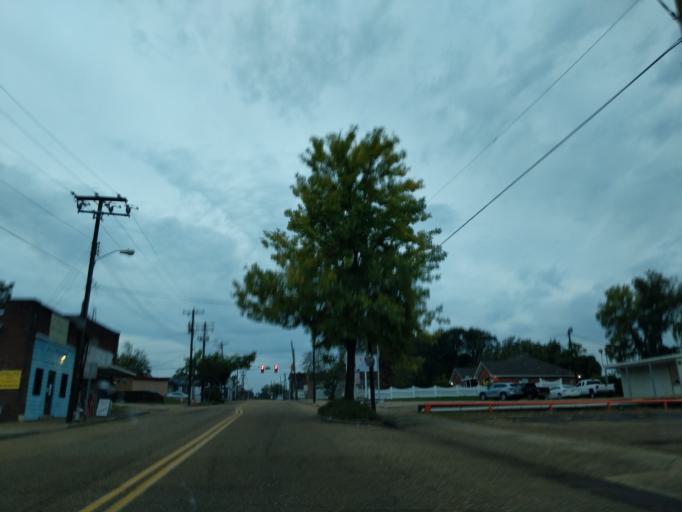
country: US
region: Mississippi
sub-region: Warren County
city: Vicksburg
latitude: 32.3439
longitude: -90.8837
